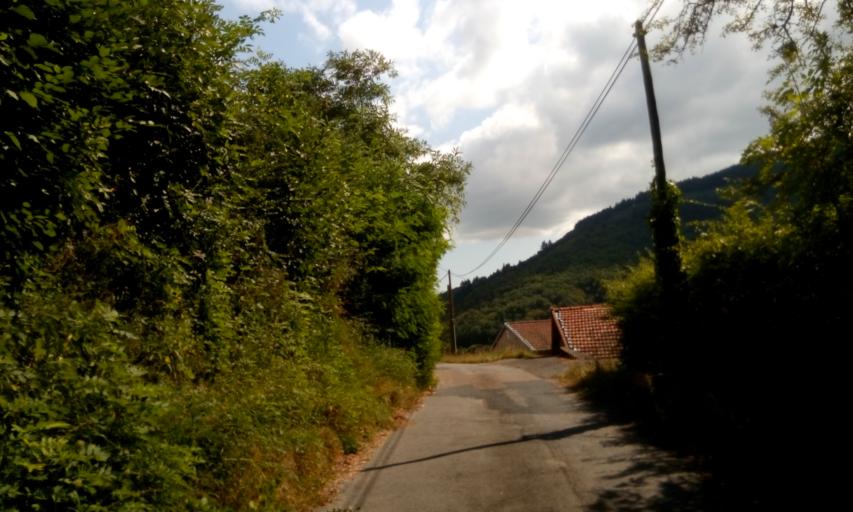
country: FR
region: Rhone-Alpes
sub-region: Departement du Rhone
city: Grandris
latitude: 46.0068
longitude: 4.4668
